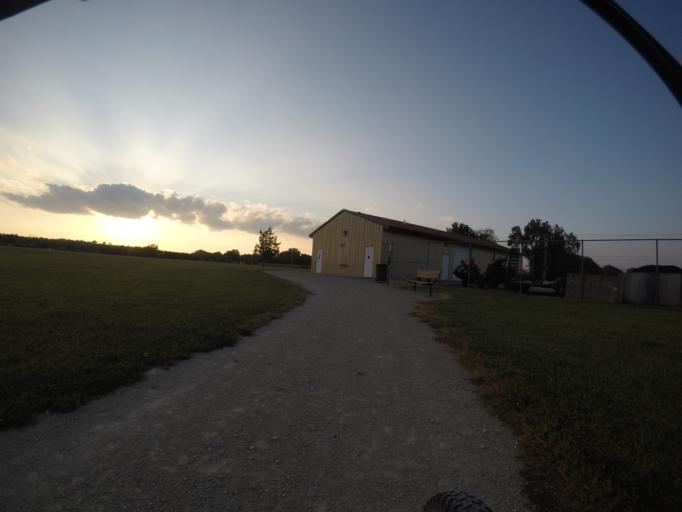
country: US
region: Kansas
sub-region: Riley County
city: Manhattan
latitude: 39.2034
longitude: -96.5447
